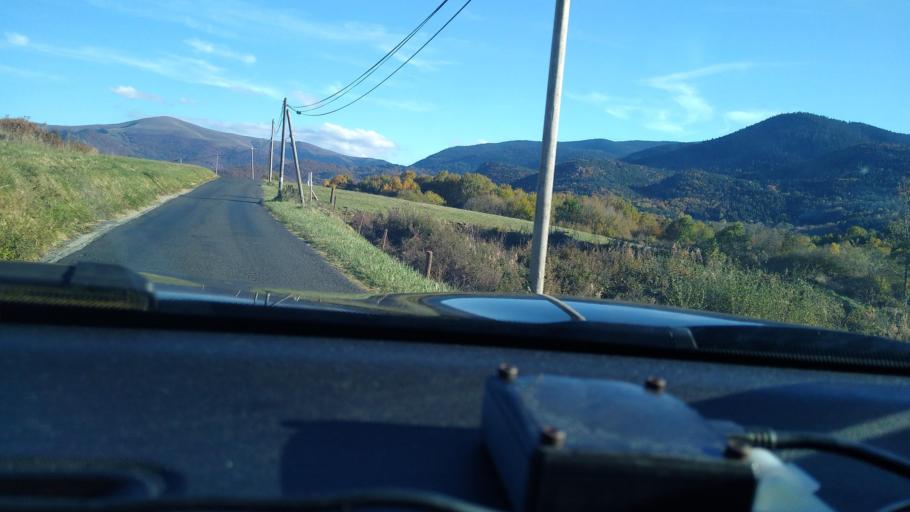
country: FR
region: Languedoc-Roussillon
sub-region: Departement de l'Aude
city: Quillan
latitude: 42.7474
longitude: 2.1727
